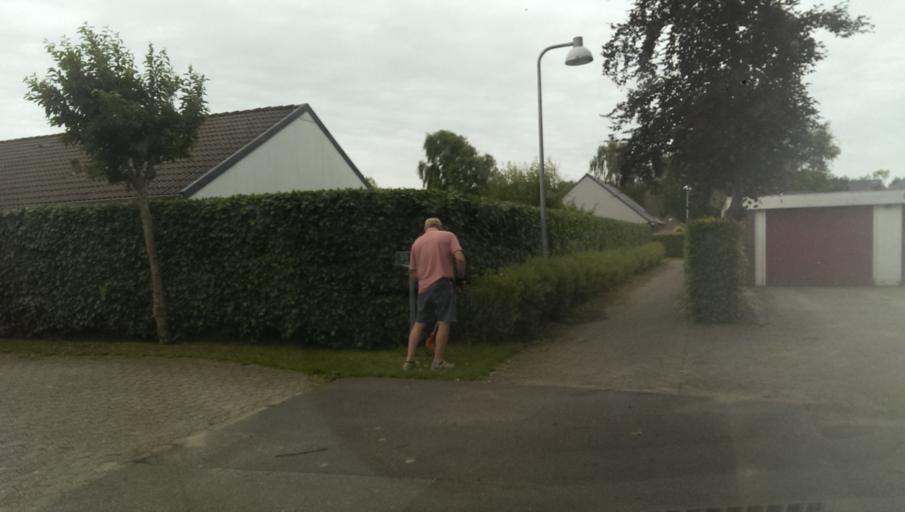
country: DK
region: South Denmark
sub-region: Esbjerg Kommune
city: Bramming
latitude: 55.4784
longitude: 8.6882
